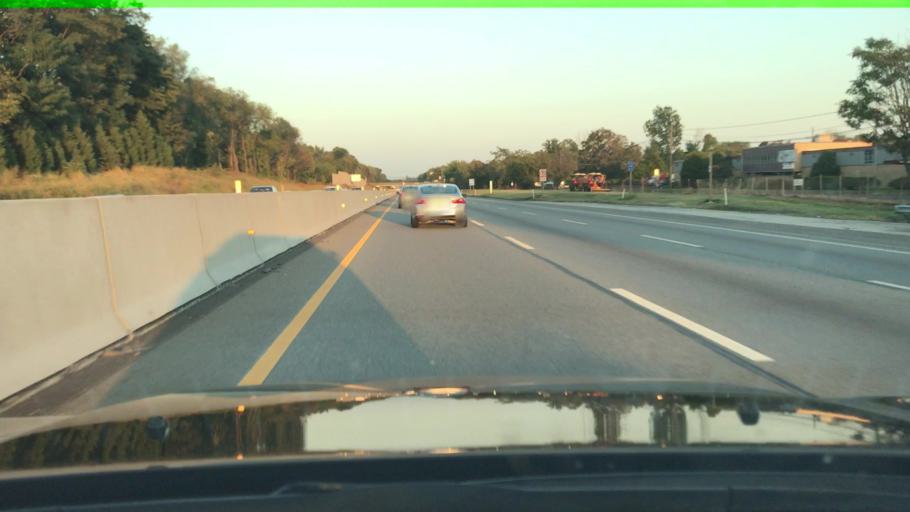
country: US
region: Pennsylvania
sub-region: Montgomery County
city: Hatboro
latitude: 40.1632
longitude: -75.0981
